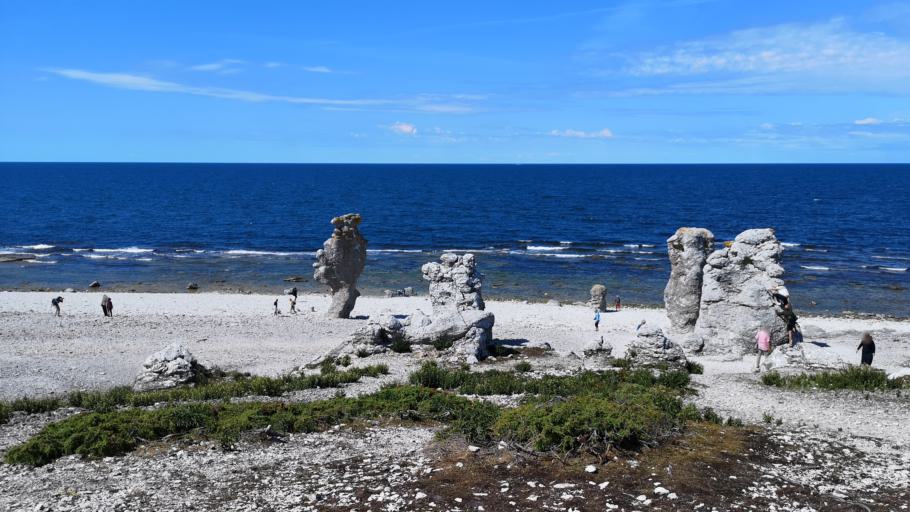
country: SE
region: Gotland
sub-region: Gotland
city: Slite
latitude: 57.9970
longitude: 19.1809
